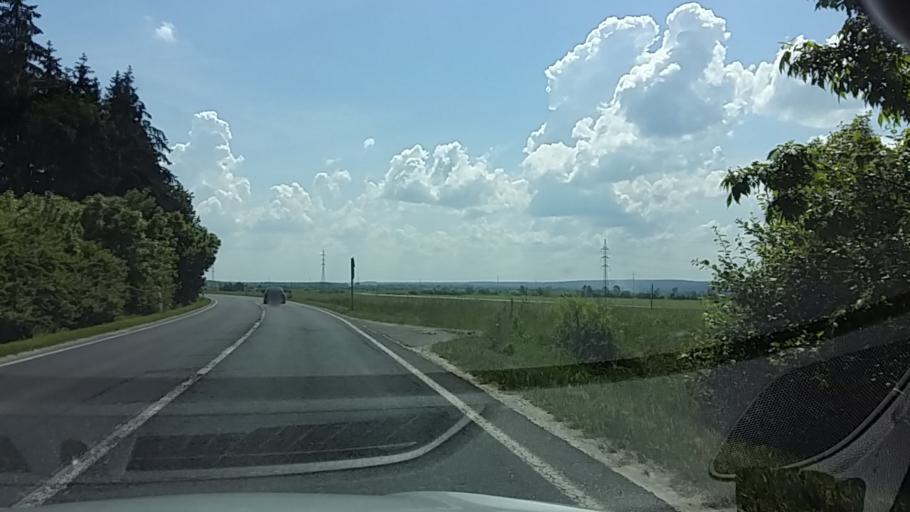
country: AT
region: Burgenland
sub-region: Politischer Bezirk Gussing
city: Inzenhof
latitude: 46.9780
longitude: 16.3333
